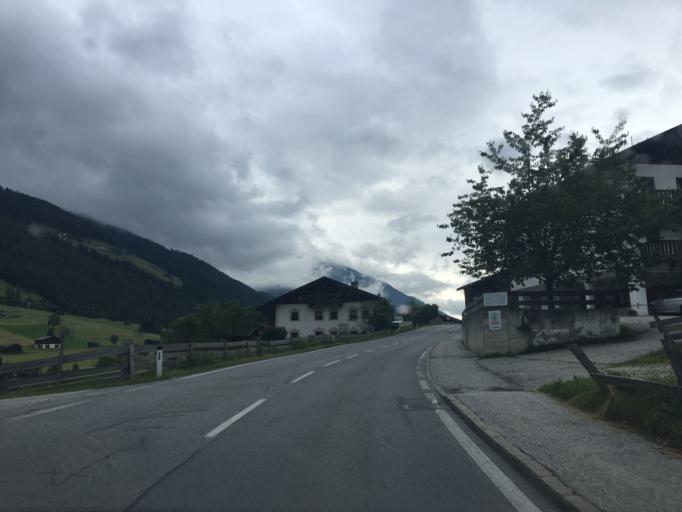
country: AT
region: Tyrol
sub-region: Politischer Bezirk Innsbruck Land
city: Neustift im Stubaital
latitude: 47.1258
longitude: 11.3332
